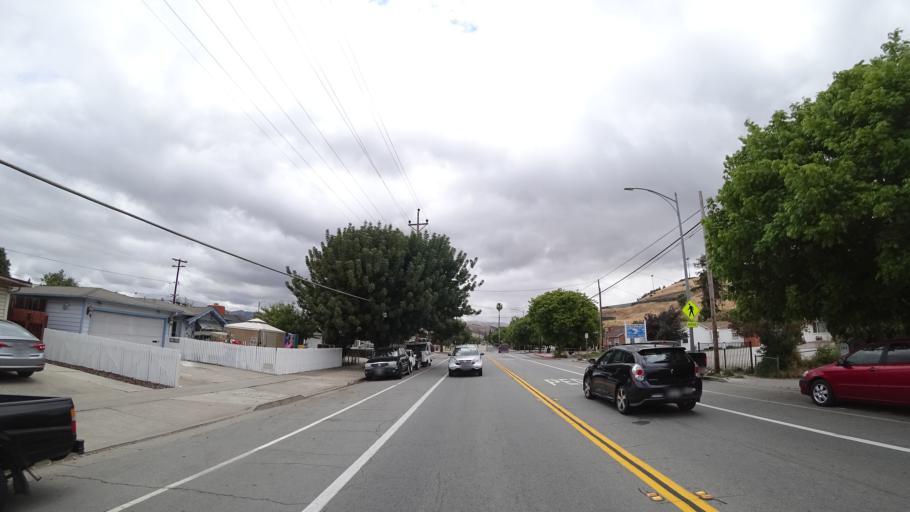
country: US
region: California
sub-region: Santa Clara County
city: Seven Trees
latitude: 37.2781
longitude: -121.8277
